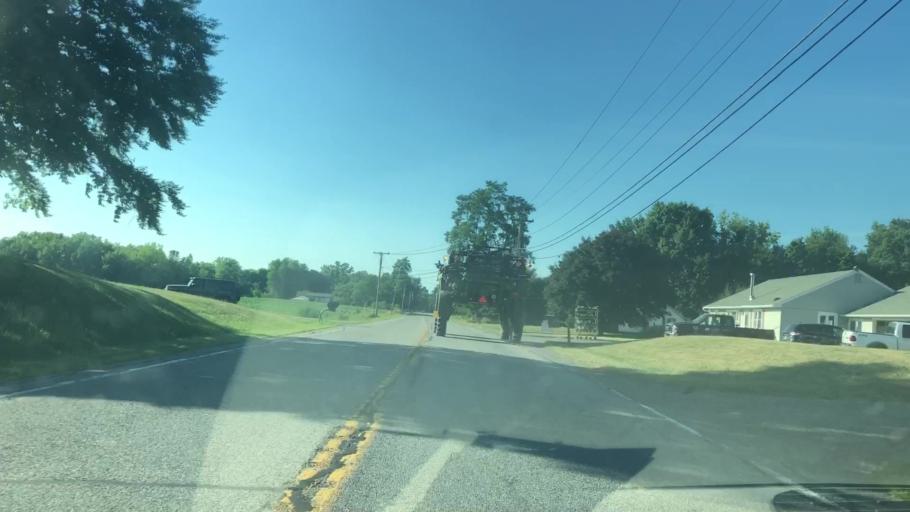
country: US
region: New York
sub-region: Wayne County
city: Ontario
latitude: 43.1922
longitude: -77.2929
